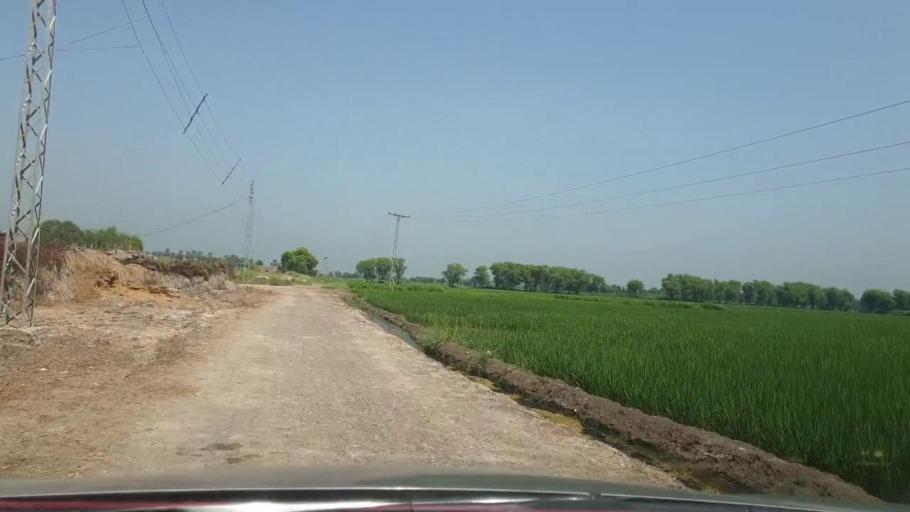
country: PK
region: Sindh
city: Kambar
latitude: 27.6122
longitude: 67.8722
